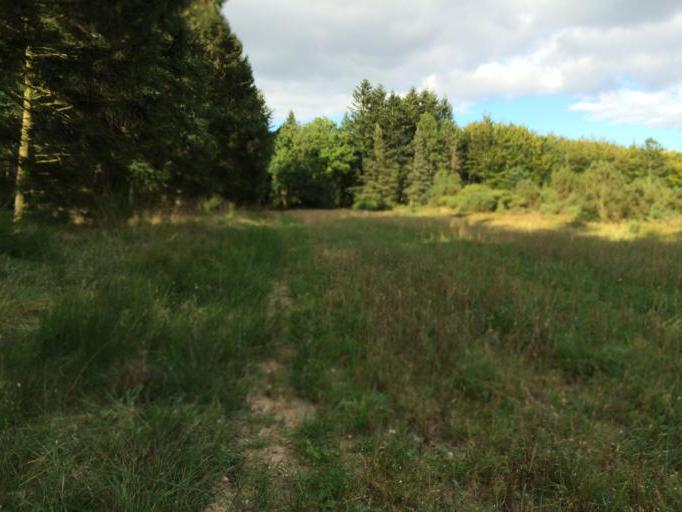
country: DK
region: Central Jutland
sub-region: Holstebro Kommune
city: Ulfborg
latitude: 56.2563
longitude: 8.4329
